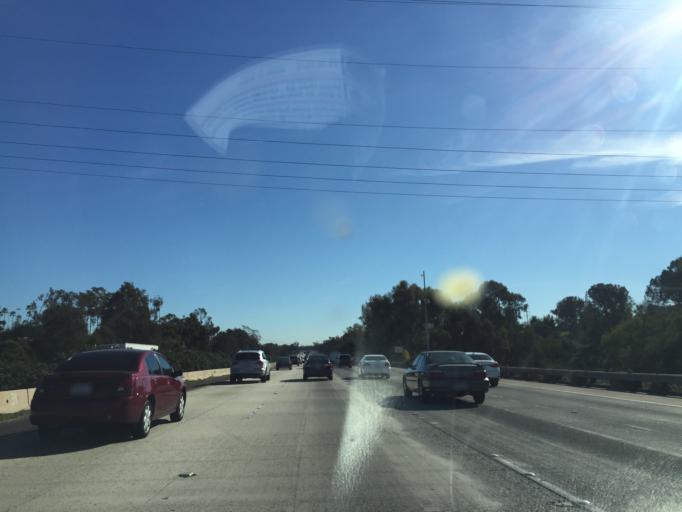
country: US
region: California
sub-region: San Diego County
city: Encinitas
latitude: 33.0562
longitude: -117.2897
